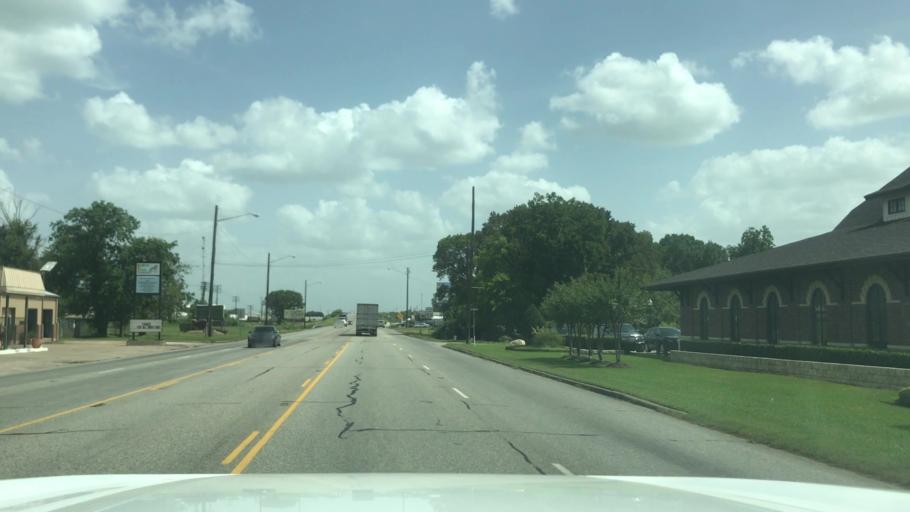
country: US
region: Texas
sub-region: Robertson County
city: Hearne
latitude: 30.8732
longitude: -96.5891
